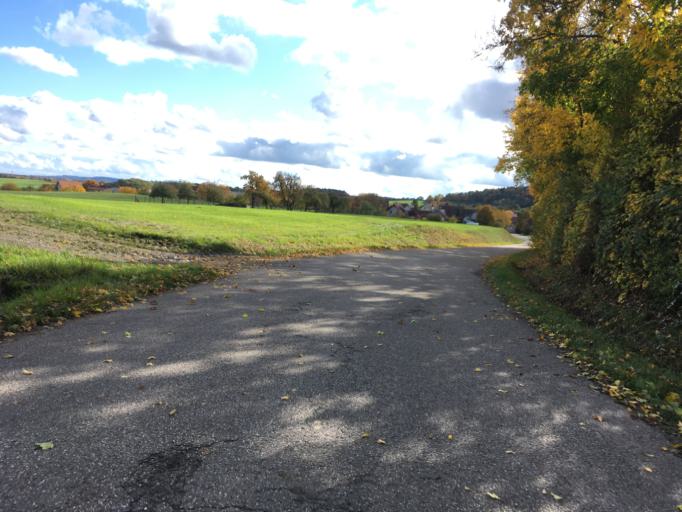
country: DE
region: Baden-Wuerttemberg
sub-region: Regierungsbezirk Stuttgart
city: Waldenburg
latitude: 49.1803
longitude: 9.6780
